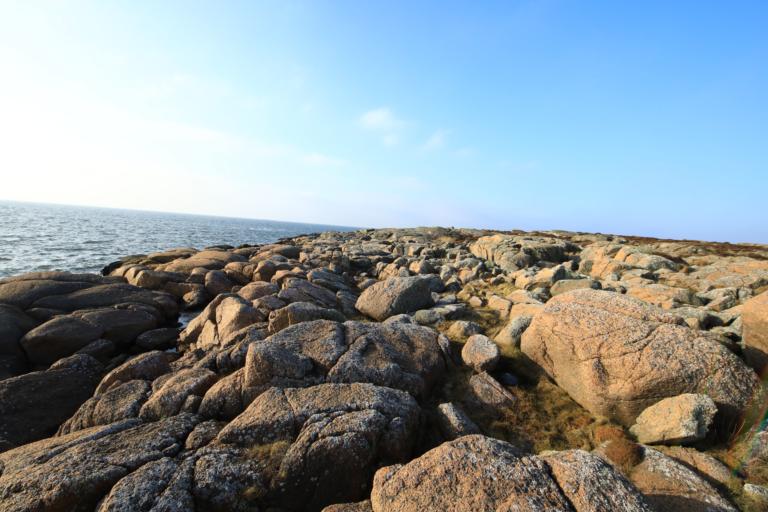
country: SE
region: Halland
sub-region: Varbergs Kommun
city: Varberg
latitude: 57.1858
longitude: 12.1630
